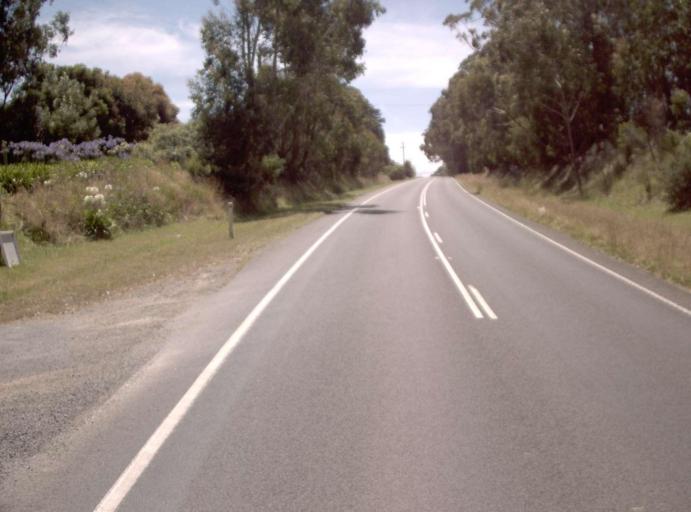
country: AU
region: Victoria
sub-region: Baw Baw
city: Warragul
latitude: -38.0407
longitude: 145.9518
